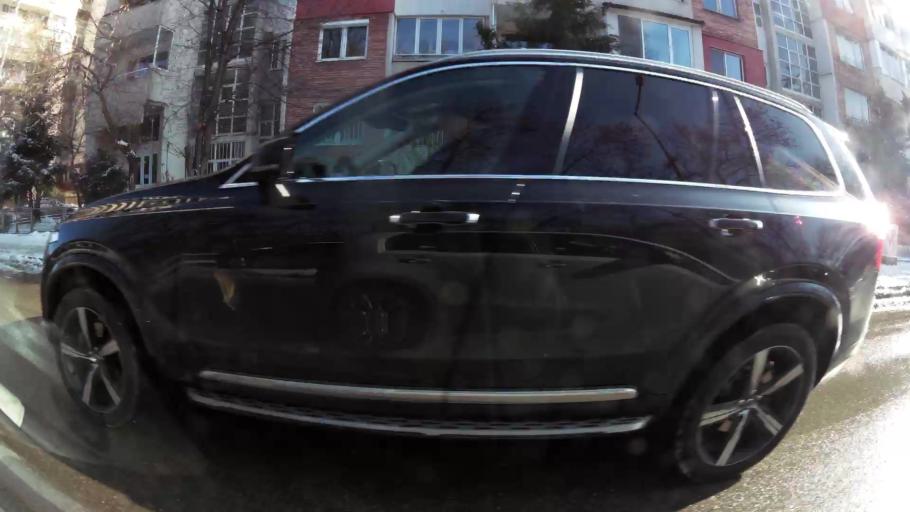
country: BG
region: Sofia-Capital
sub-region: Stolichna Obshtina
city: Sofia
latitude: 42.6624
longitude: 23.3136
